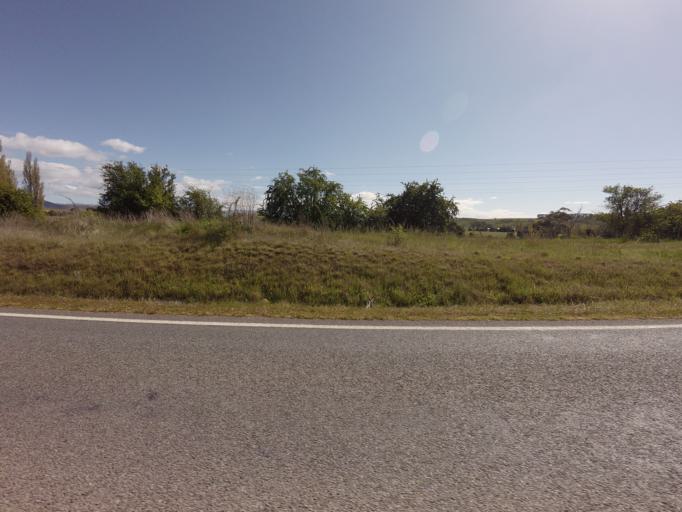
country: AU
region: Tasmania
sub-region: Derwent Valley
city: New Norfolk
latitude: -42.6876
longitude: 146.9419
